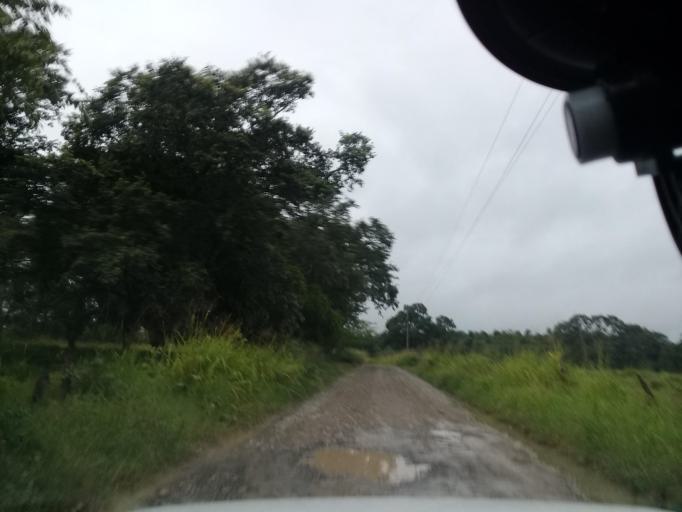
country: MX
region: Veracruz
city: Platon Sanchez
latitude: 21.2461
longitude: -98.3462
